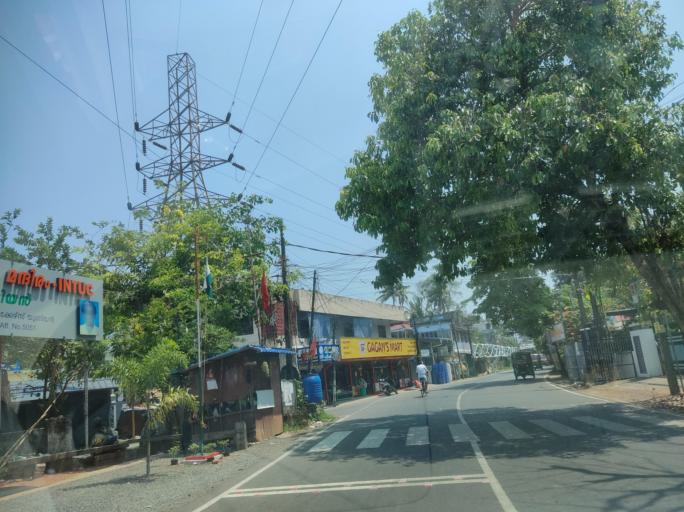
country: IN
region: Kerala
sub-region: Ernakulam
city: Cochin
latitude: 9.8977
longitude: 76.2840
